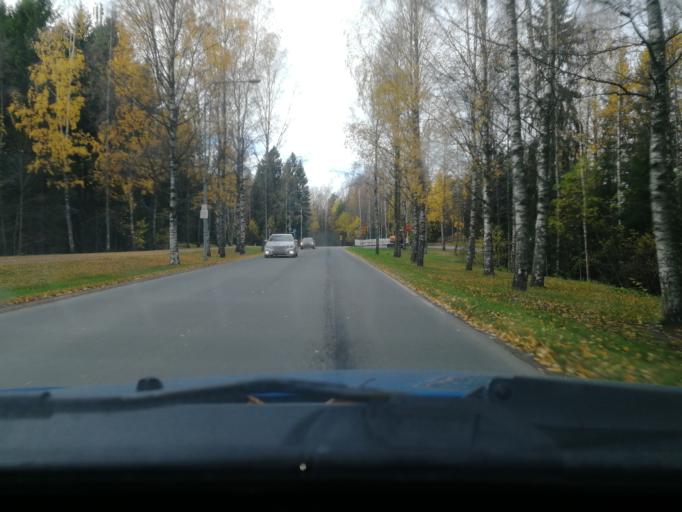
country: FI
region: Pirkanmaa
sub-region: Tampere
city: Tampere
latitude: 61.4491
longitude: 23.8330
